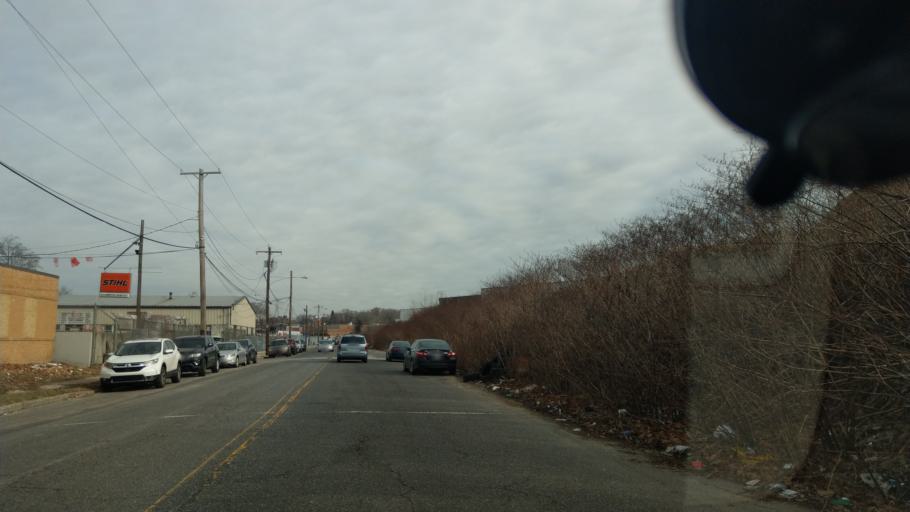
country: US
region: Pennsylvania
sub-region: Montgomery County
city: Rockledge
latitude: 40.0144
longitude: -75.1204
